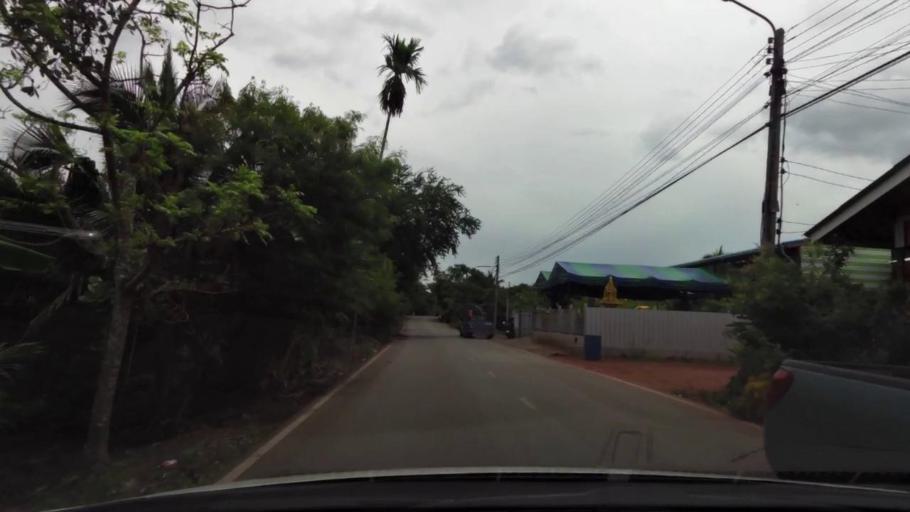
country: TH
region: Ratchaburi
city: Damnoen Saduak
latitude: 13.5493
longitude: 100.0192
